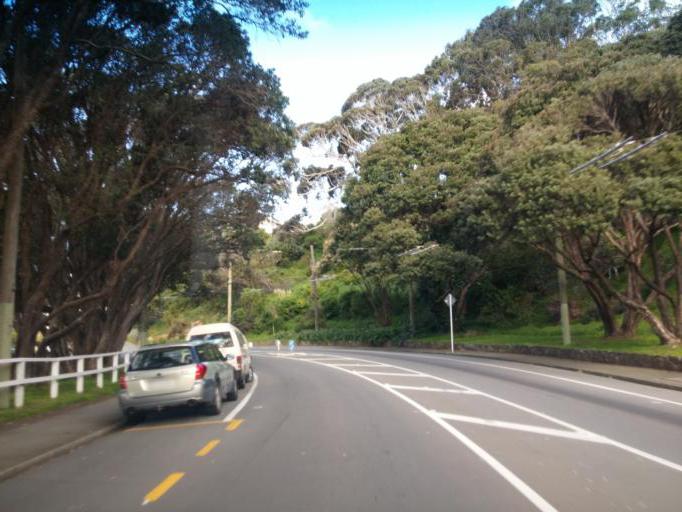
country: NZ
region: Wellington
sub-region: Wellington City
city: Wellington
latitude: -41.3134
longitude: 174.7896
